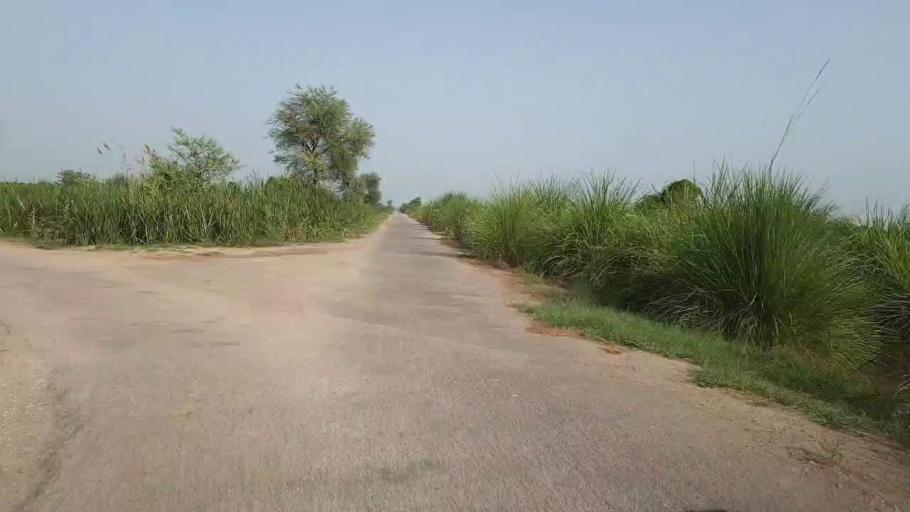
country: PK
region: Sindh
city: Daur
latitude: 26.3493
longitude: 68.1747
